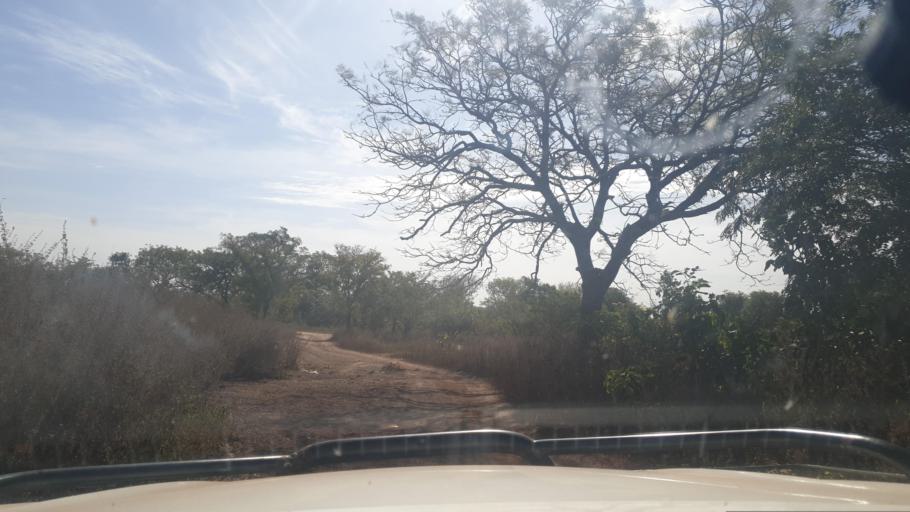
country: GN
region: Kankan
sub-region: Mandiana Prefecture
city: Mandiana
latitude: 10.4873
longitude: -8.0954
